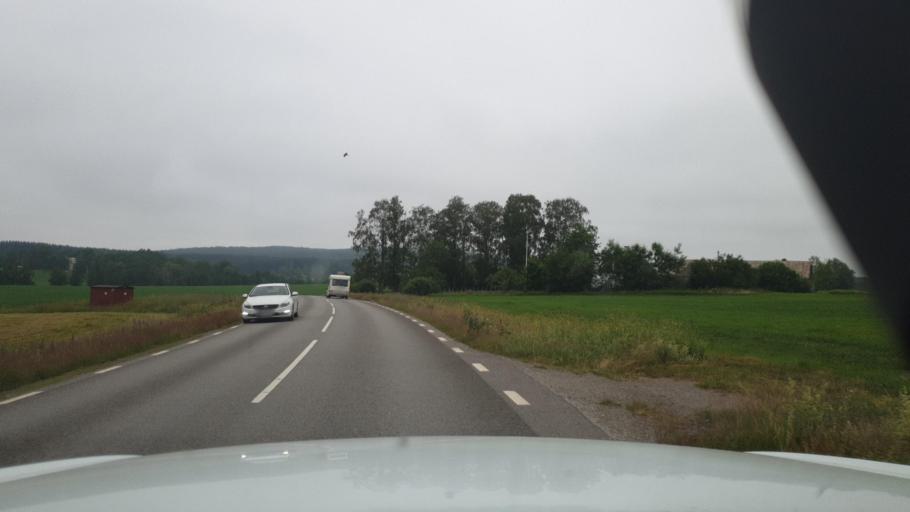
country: SE
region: Vaermland
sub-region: Arvika Kommun
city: Arvika
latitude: 59.7510
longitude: 12.5528
